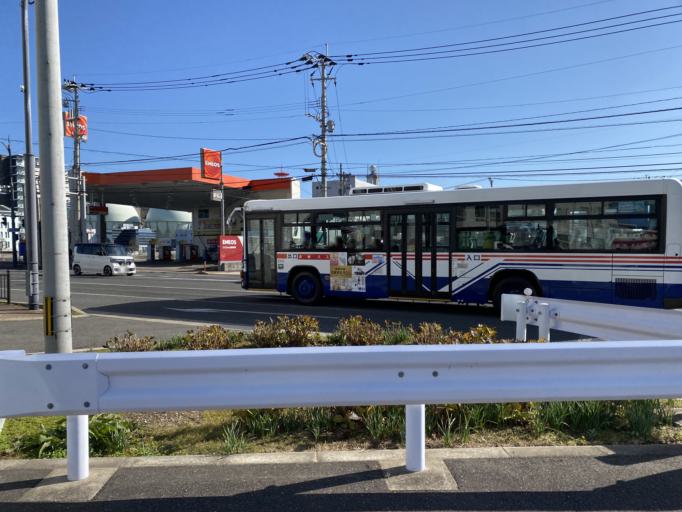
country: JP
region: Nagasaki
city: Nagasaki-shi
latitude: 32.7563
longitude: 129.8637
